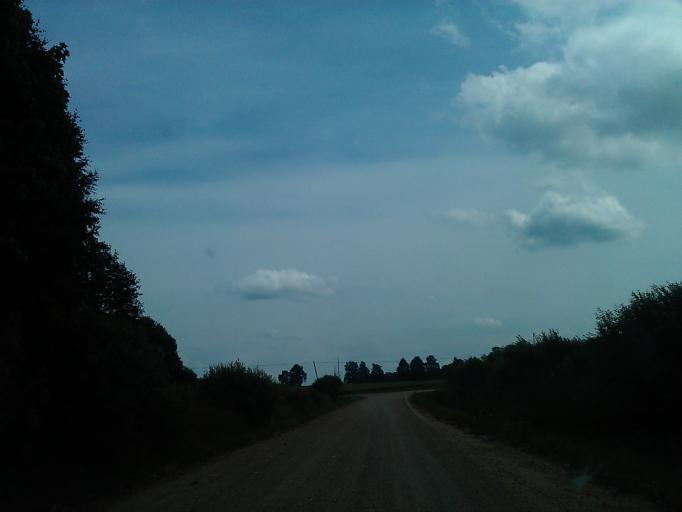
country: LV
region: Burtnieki
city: Matisi
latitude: 57.7105
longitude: 25.1503
